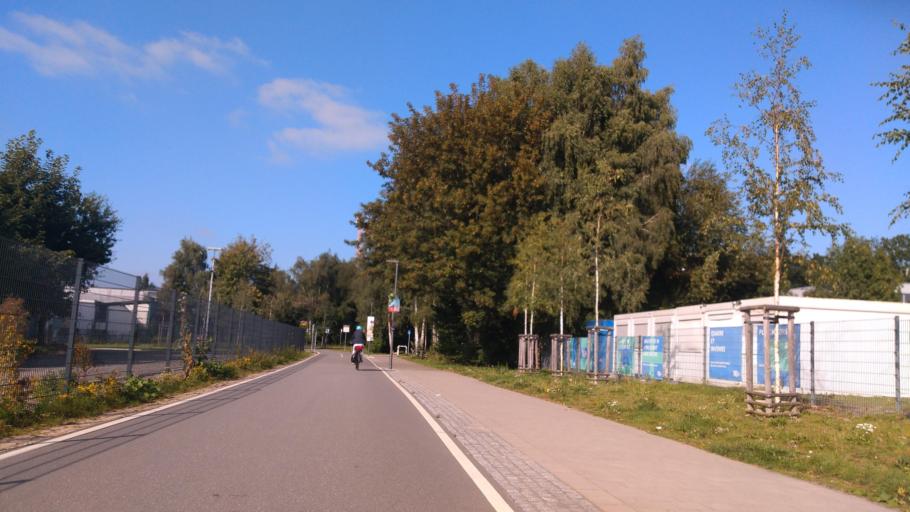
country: DE
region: Schleswig-Holstein
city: Kiel
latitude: 54.3354
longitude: 10.1183
